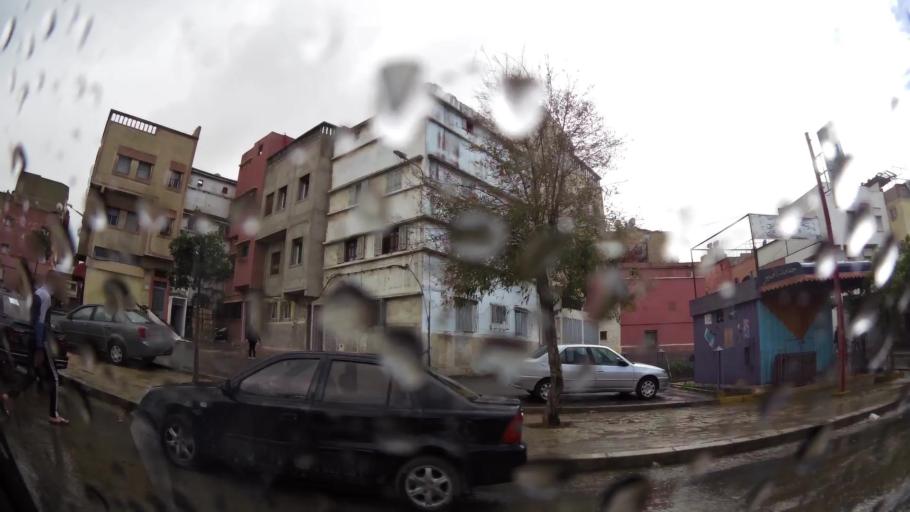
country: MA
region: Grand Casablanca
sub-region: Mediouna
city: Tit Mellil
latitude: 33.5551
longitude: -7.5489
